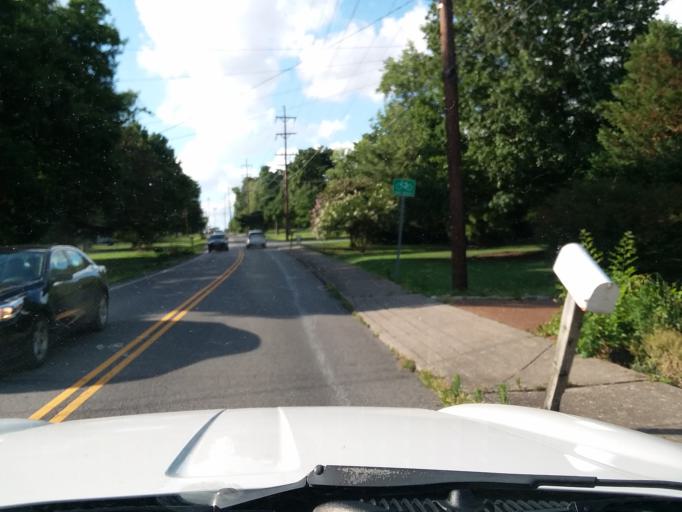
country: US
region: Tennessee
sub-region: Davidson County
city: Oak Hill
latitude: 36.0710
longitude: -86.7587
